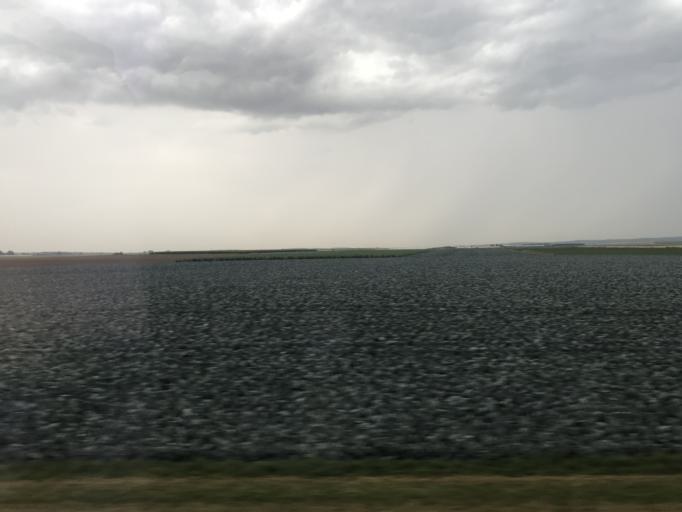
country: DE
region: Bavaria
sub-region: Regierungsbezirk Unterfranken
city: Oberpleichfeld
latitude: 49.8908
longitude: 10.0823
